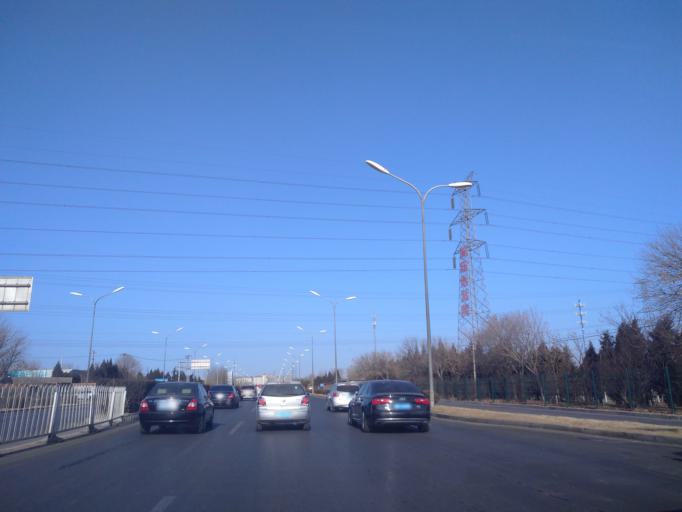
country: CN
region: Beijing
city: Jiugong
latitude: 39.8147
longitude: 116.4851
